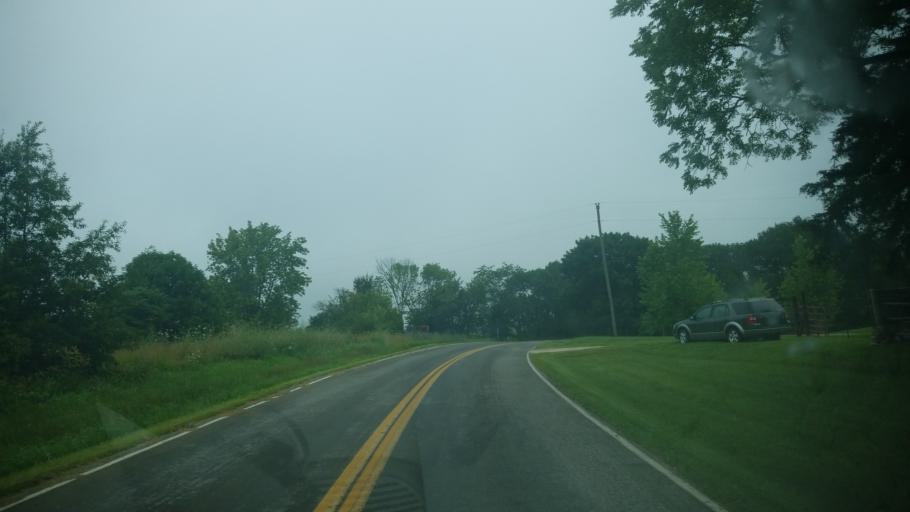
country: US
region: Missouri
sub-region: Audrain County
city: Vandalia
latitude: 39.3011
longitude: -91.3505
